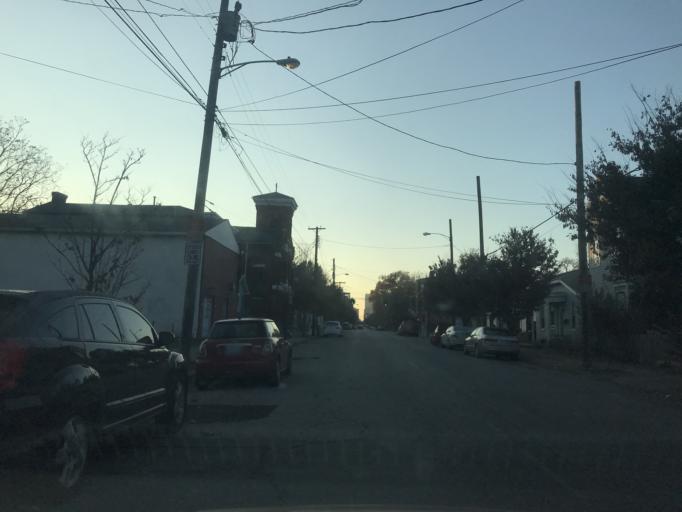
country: US
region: Kentucky
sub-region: Jefferson County
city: Louisville
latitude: 38.2488
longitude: -85.7356
